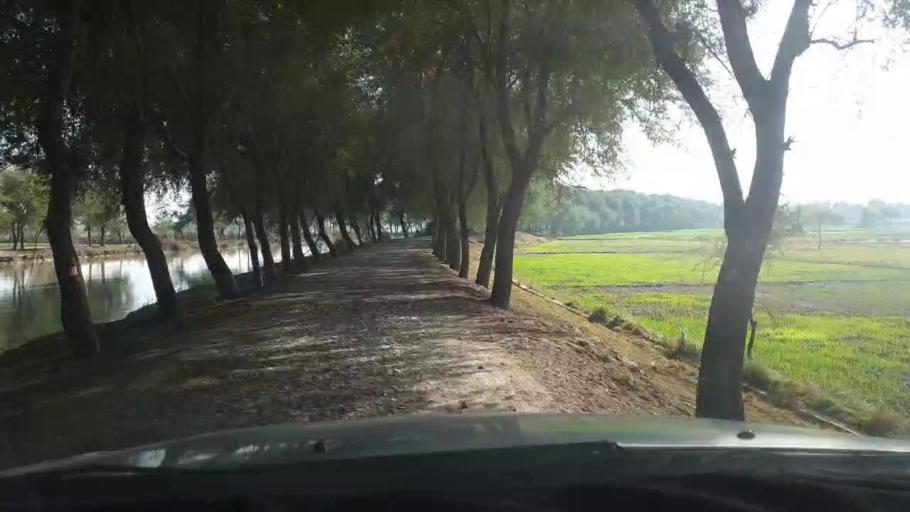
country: PK
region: Sindh
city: Mirpur Mathelo
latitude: 27.9872
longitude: 69.5449
